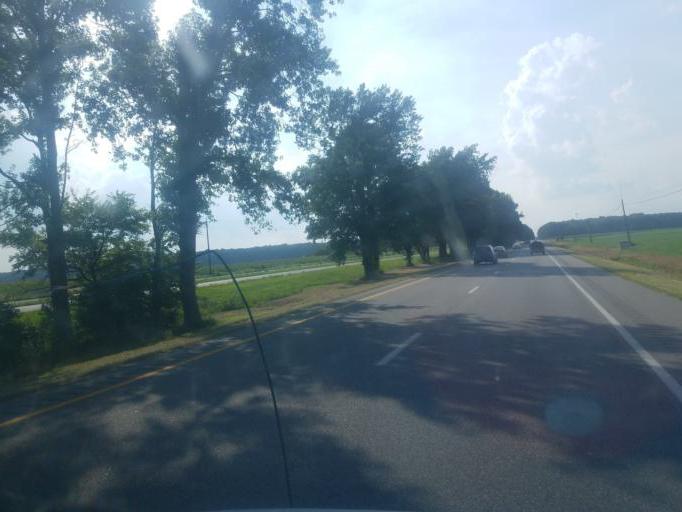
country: US
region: Maryland
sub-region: Worcester County
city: Berlin
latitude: 38.3534
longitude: -75.2409
